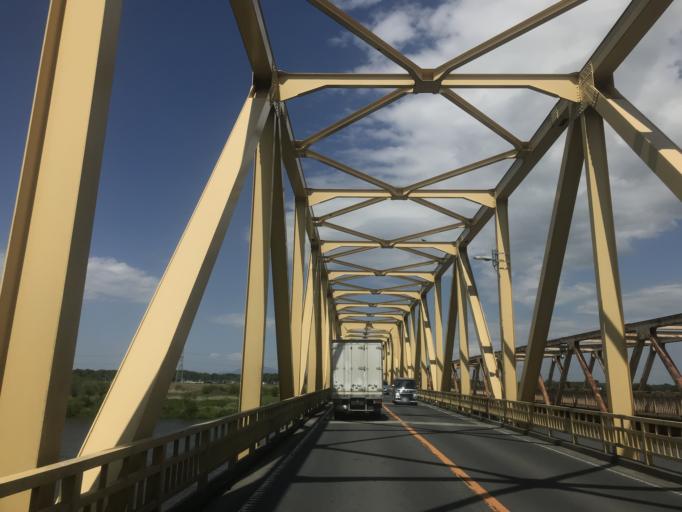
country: JP
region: Chiba
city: Noda
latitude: 35.9829
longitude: 139.8905
